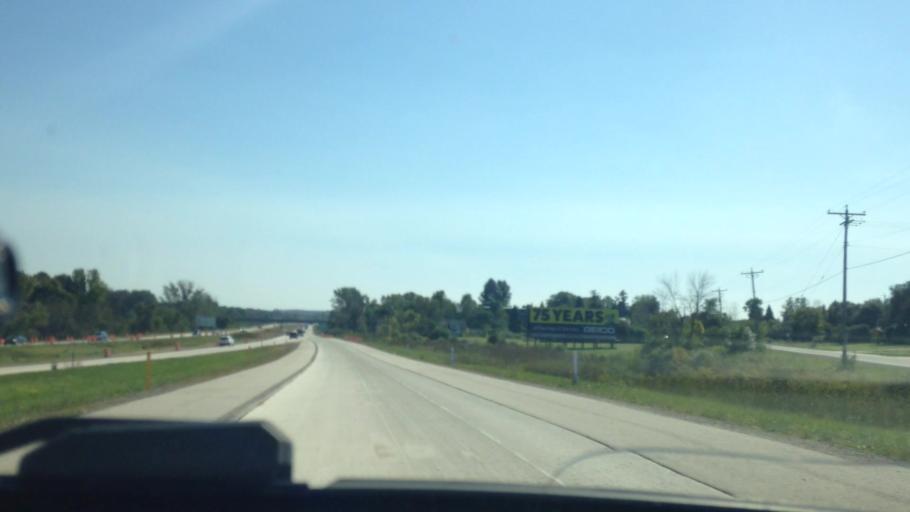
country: US
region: Wisconsin
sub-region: Ozaukee County
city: Grafton
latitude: 43.3368
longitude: -87.9252
